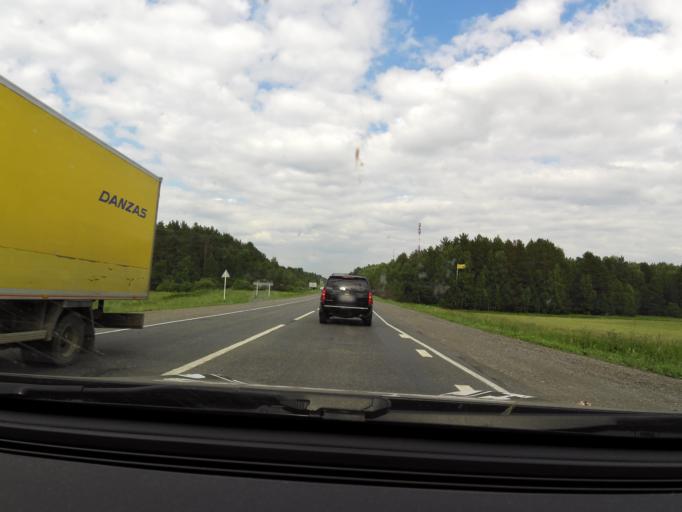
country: RU
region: Sverdlovsk
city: Druzhinino
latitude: 56.8010
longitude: 59.4718
